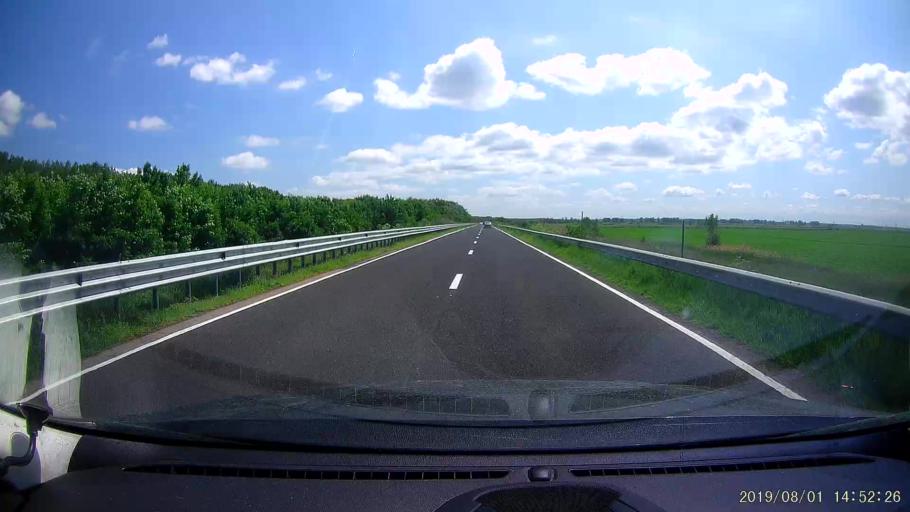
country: RO
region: Braila
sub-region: Comuna Vadeni
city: Vadeni
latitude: 45.3551
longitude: 28.0108
